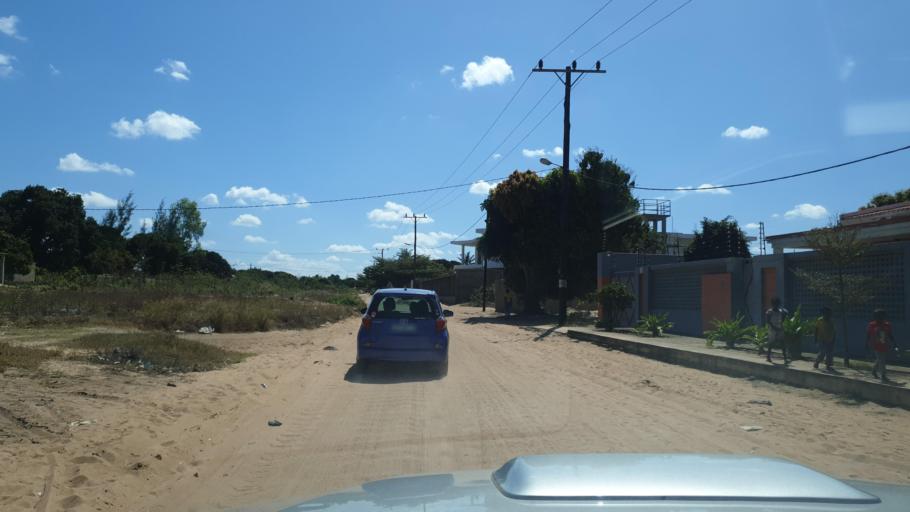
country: MZ
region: Nampula
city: Nampula
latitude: -15.1058
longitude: 39.2062
